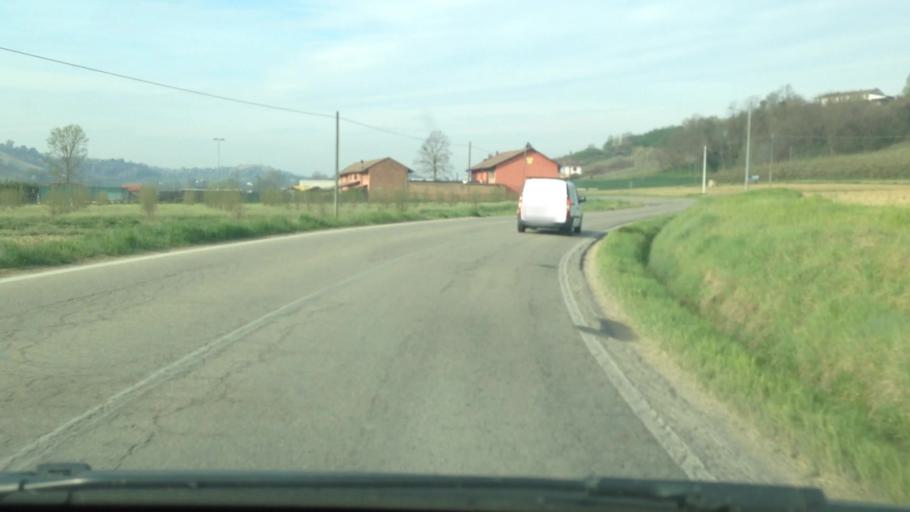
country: IT
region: Piedmont
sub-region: Provincia di Asti
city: San Damiano d'Asti
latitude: 44.8108
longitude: 8.0395
